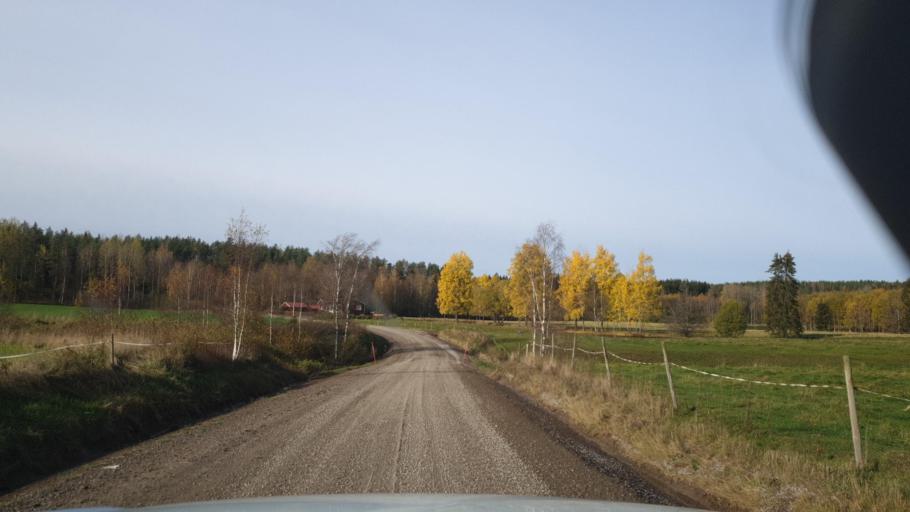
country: SE
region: Vaermland
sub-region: Eda Kommun
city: Charlottenberg
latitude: 59.7285
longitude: 12.1399
